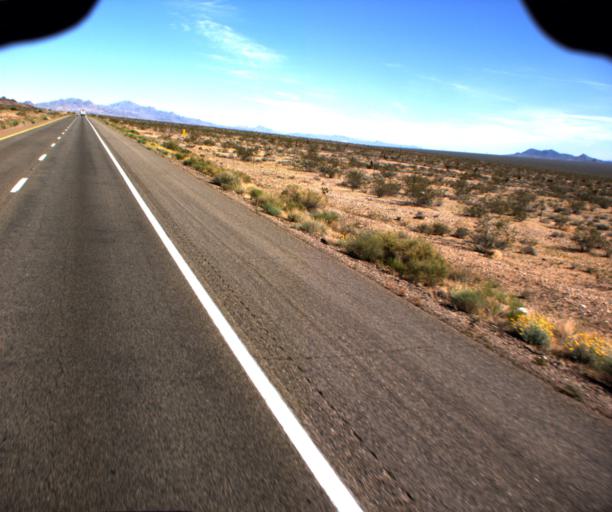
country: US
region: Arizona
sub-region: Mohave County
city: Dolan Springs
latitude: 35.7445
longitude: -114.4984
